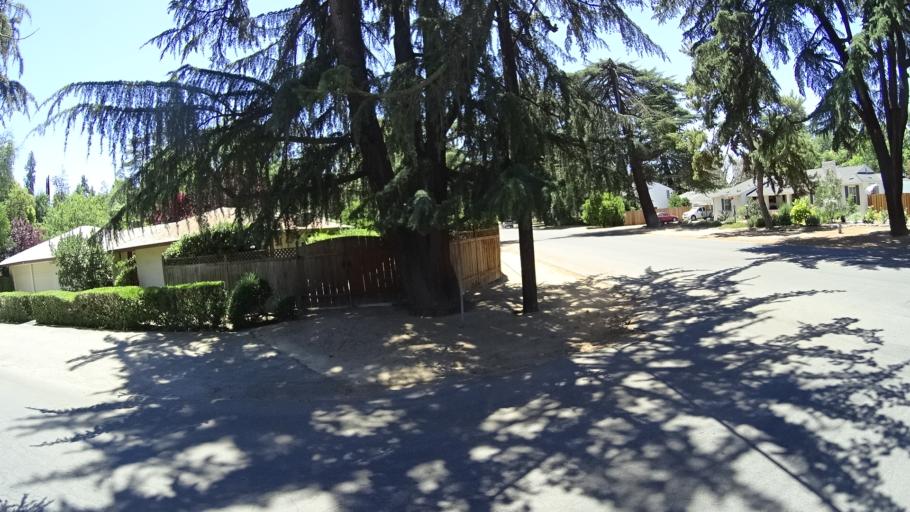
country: US
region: California
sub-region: Fresno County
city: Fresno
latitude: 36.7831
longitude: -119.8022
